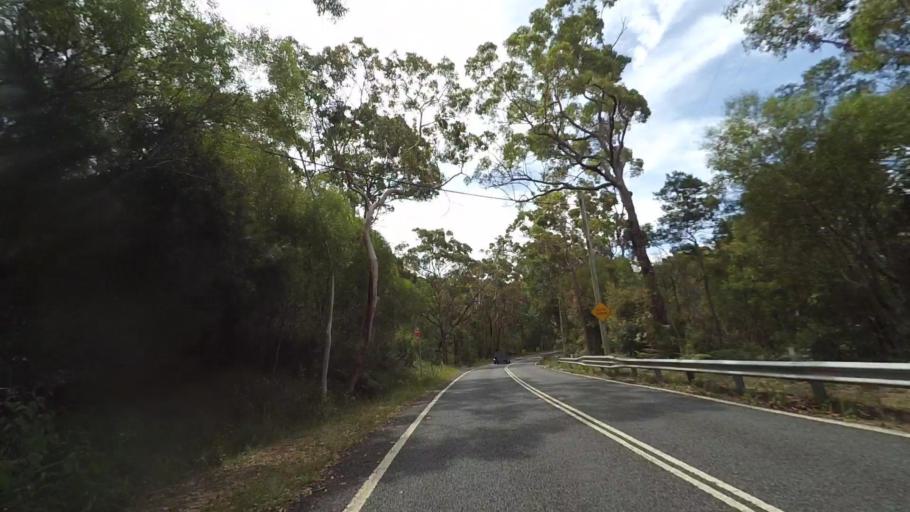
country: AU
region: New South Wales
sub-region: Sutherland Shire
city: Loftus
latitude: -34.0701
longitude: 151.0572
